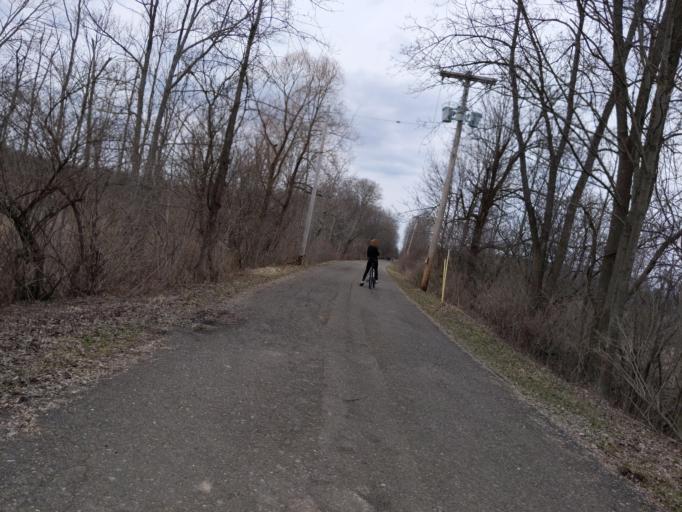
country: US
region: New York
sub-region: Tompkins County
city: Dryden
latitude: 42.5067
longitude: -76.3427
